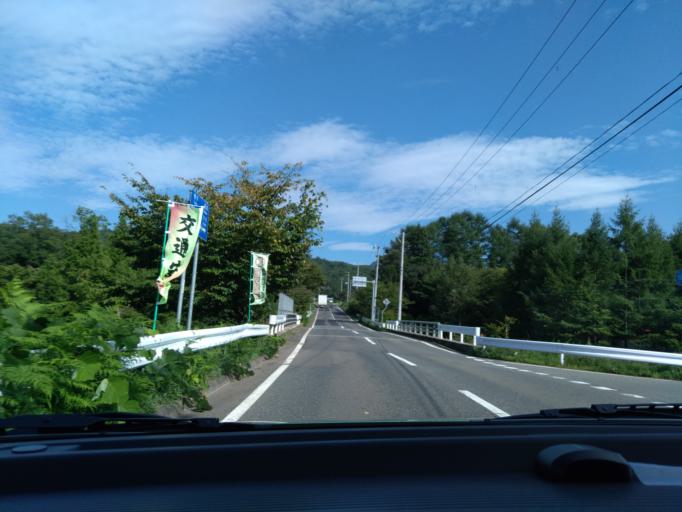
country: JP
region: Iwate
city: Shizukuishi
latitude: 39.6441
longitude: 140.9974
